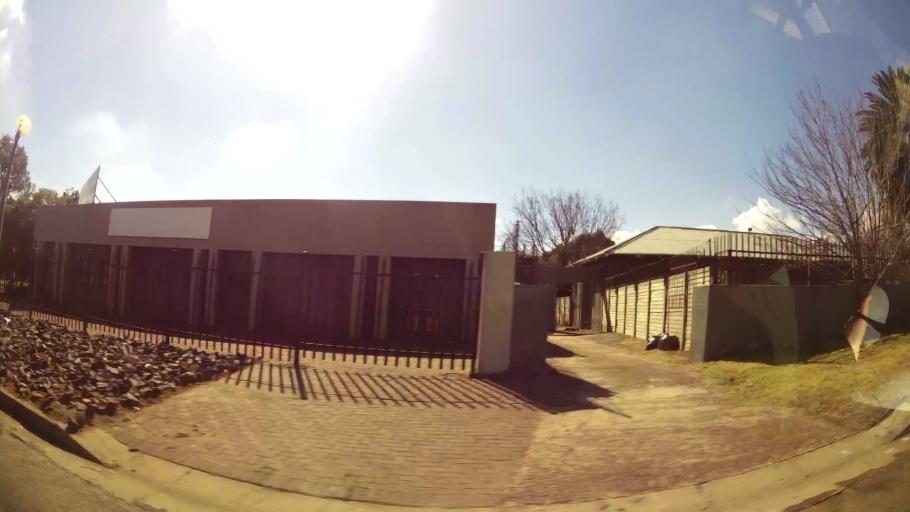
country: ZA
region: Mpumalanga
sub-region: Nkangala District Municipality
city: Witbank
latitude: -25.8847
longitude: 29.2191
